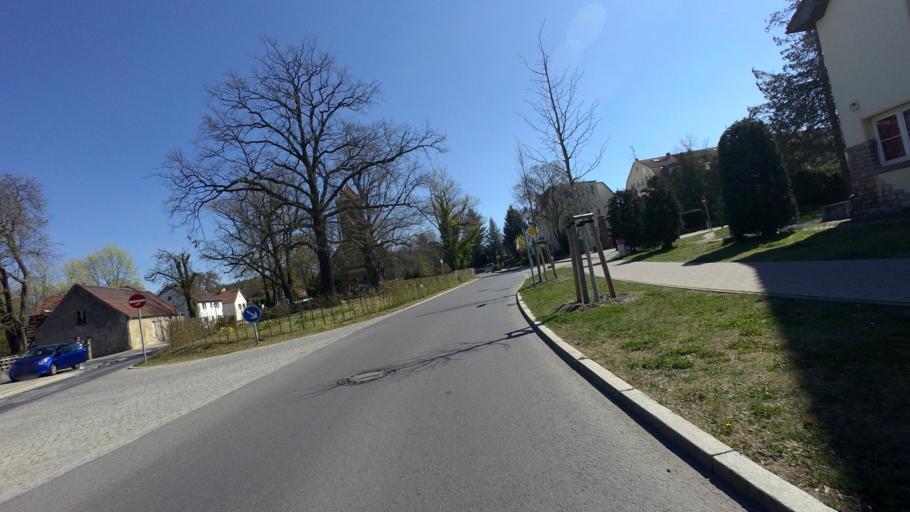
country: DE
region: Brandenburg
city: Zeuthen
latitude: 52.3407
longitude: 13.6126
